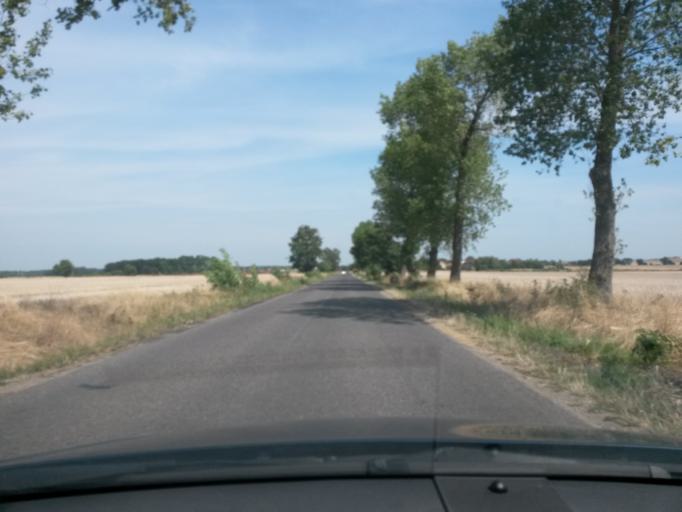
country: PL
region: Lower Silesian Voivodeship
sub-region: Powiat legnicki
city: Prochowice
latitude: 51.2080
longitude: 16.3480
